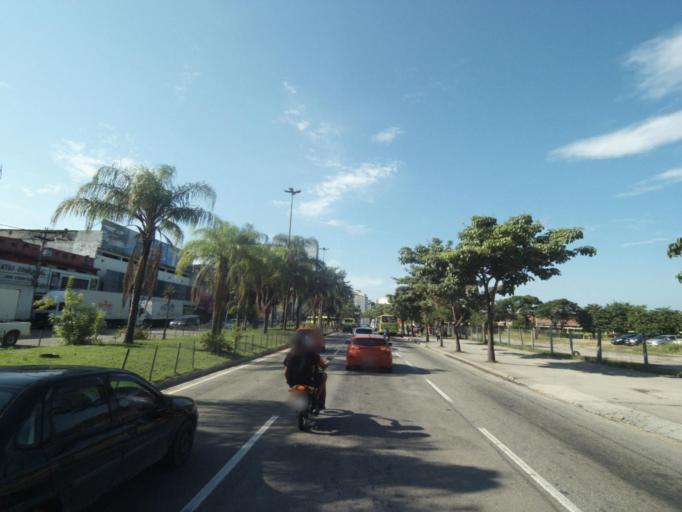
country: BR
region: Rio de Janeiro
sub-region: Niteroi
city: Niteroi
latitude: -22.8888
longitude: -43.1245
